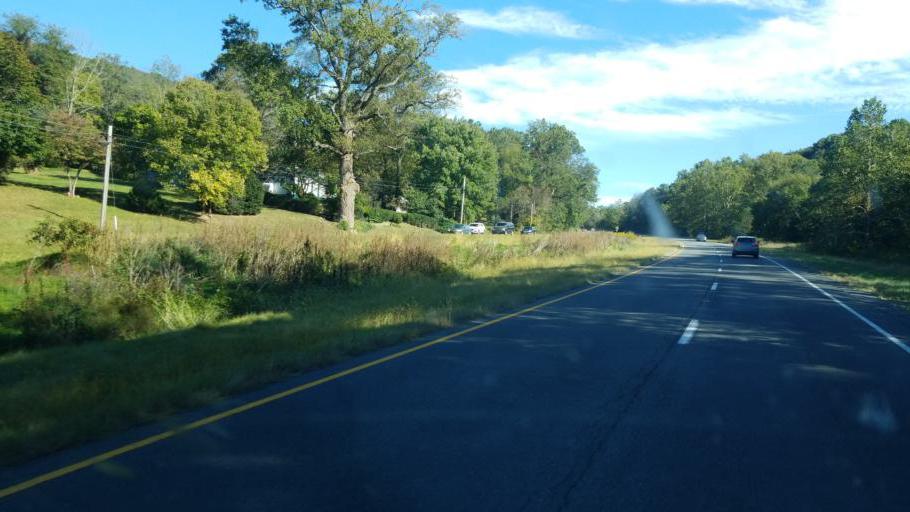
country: US
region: Virginia
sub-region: Warren County
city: Shenandoah Farms
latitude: 39.0213
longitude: -77.9726
